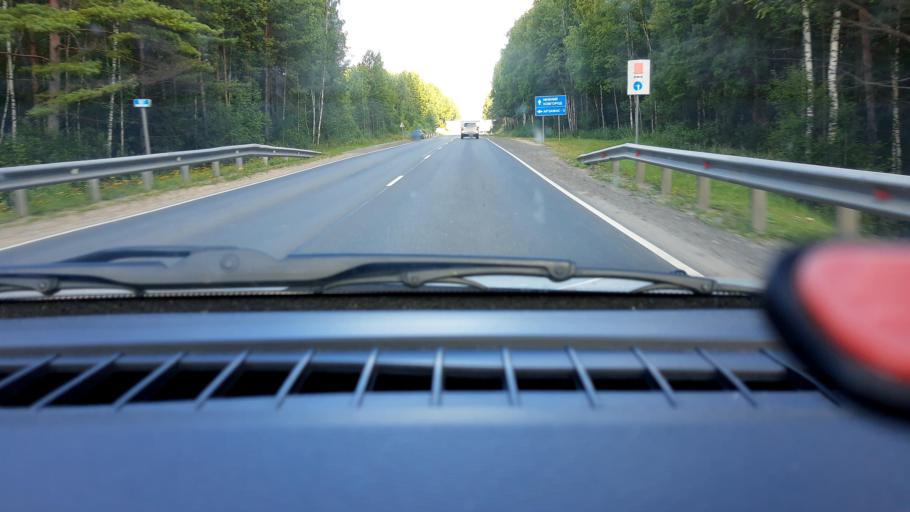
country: RU
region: Nizjnij Novgorod
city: Arzamas
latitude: 55.4280
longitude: 43.9040
